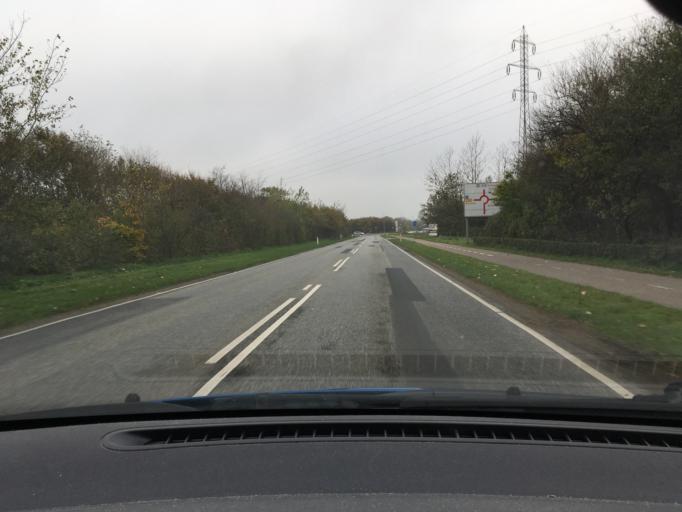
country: DK
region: South Denmark
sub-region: Tonder Kommune
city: Tonder
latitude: 54.9520
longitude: 8.8924
